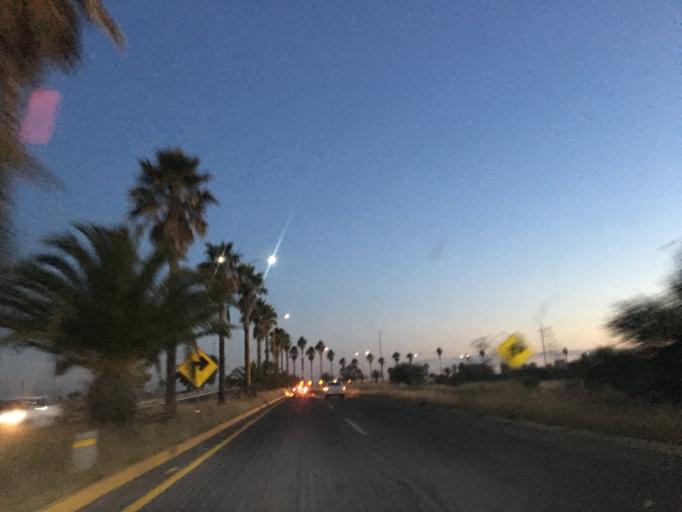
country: MX
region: Aguascalientes
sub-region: Aguascalientes
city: Penuelas (El Cienegal)
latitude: 21.7227
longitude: -102.3100
